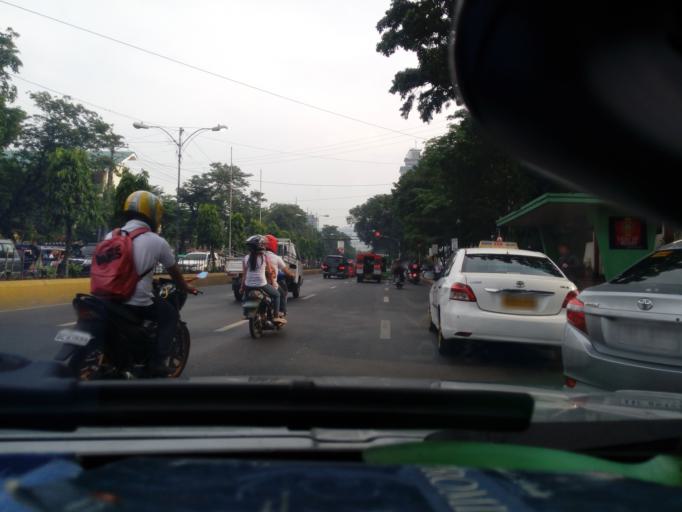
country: PH
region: Central Visayas
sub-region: Cebu City
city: Calero
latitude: 10.3013
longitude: 123.8963
